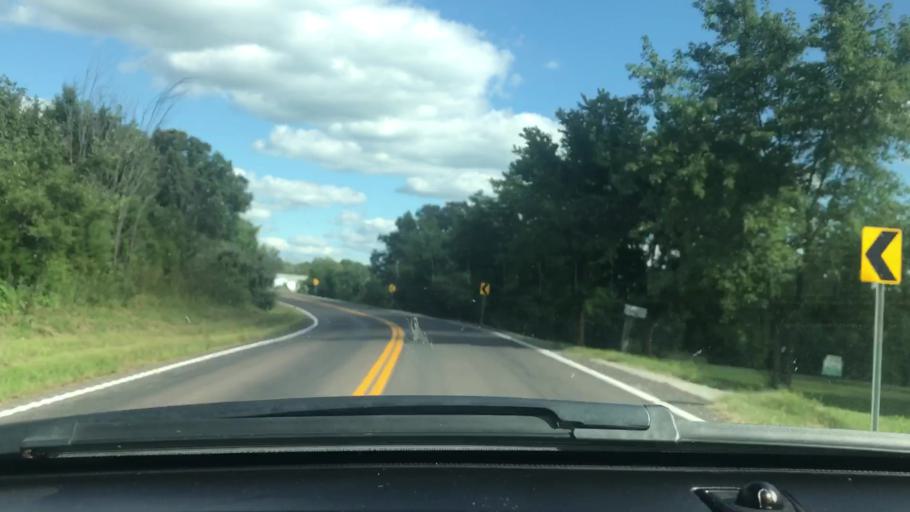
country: US
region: Missouri
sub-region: Wright County
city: Mountain Grove
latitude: 37.2548
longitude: -92.3066
